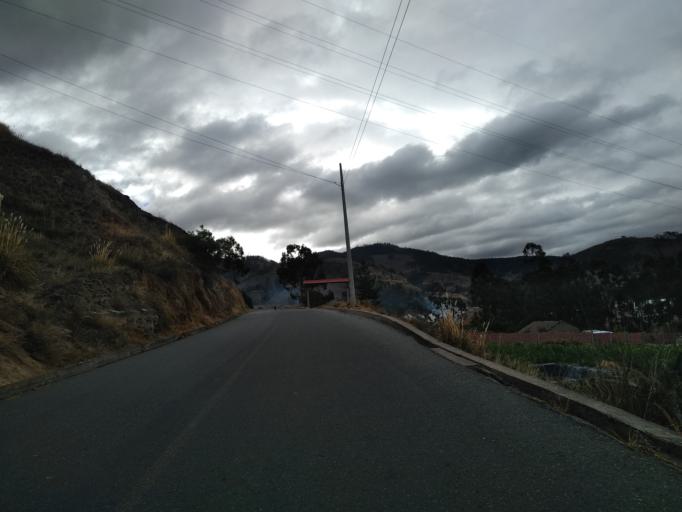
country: EC
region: Chimborazo
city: Riobamba
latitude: -1.6851
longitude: -78.6822
